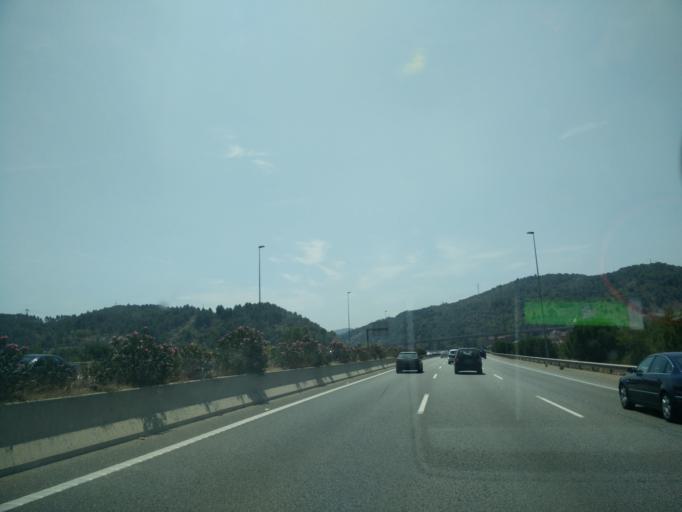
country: ES
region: Catalonia
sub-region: Provincia de Barcelona
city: Martorell
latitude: 41.4820
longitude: 1.9358
